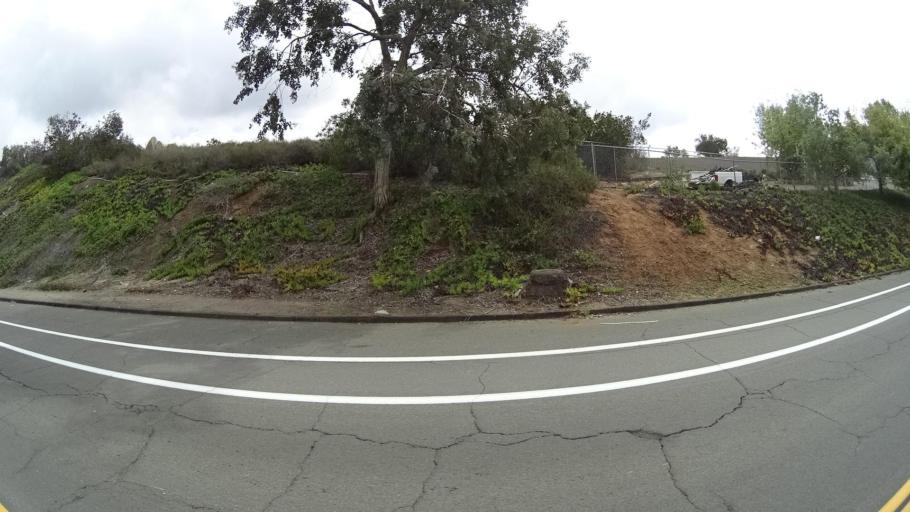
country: US
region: California
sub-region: San Diego County
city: Rancho San Diego
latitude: 32.7686
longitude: -116.9107
